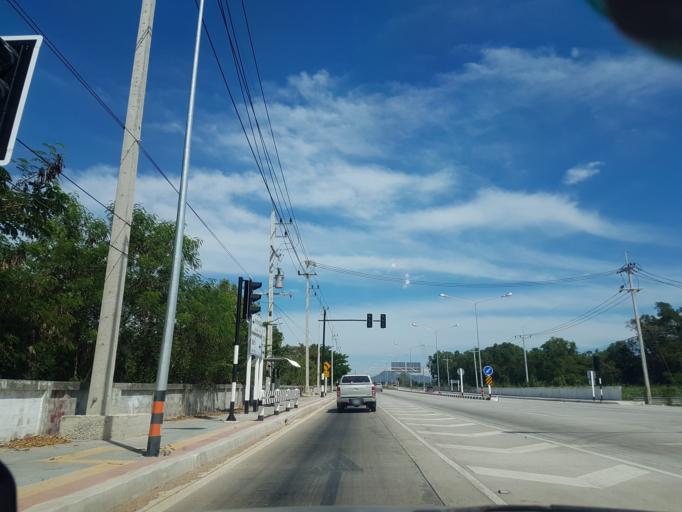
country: TH
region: Chon Buri
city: Sattahip
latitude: 12.6695
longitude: 100.9750
